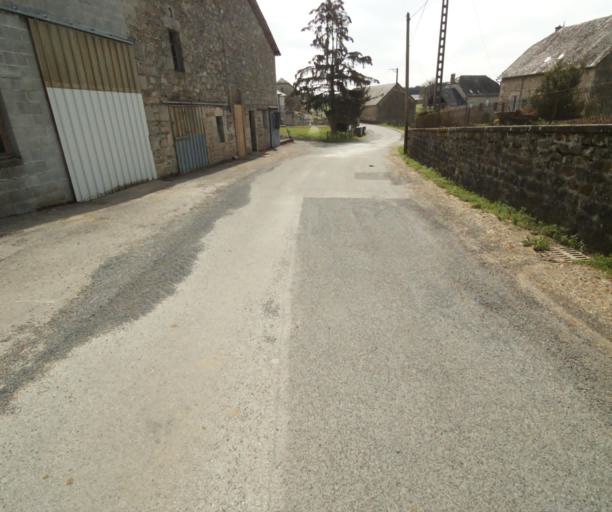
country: FR
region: Limousin
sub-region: Departement de la Correze
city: Correze
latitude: 45.3535
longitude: 1.8848
